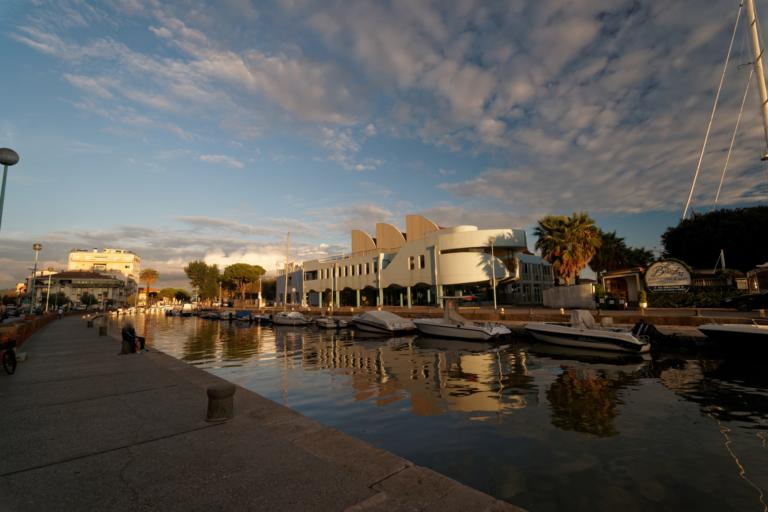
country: IT
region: Tuscany
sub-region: Provincia di Lucca
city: Viareggio
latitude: 43.8651
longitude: 10.2448
